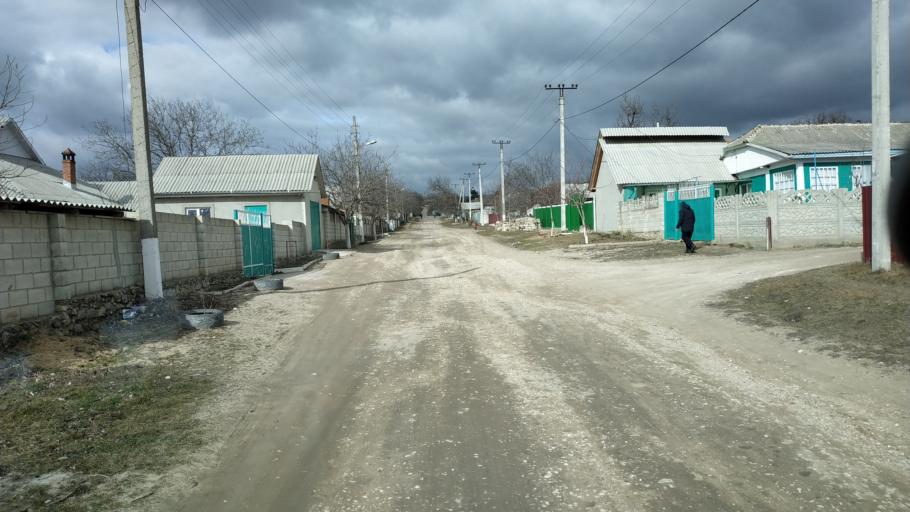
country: MD
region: Stinga Nistrului
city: Bucovat
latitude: 47.2246
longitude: 28.4417
